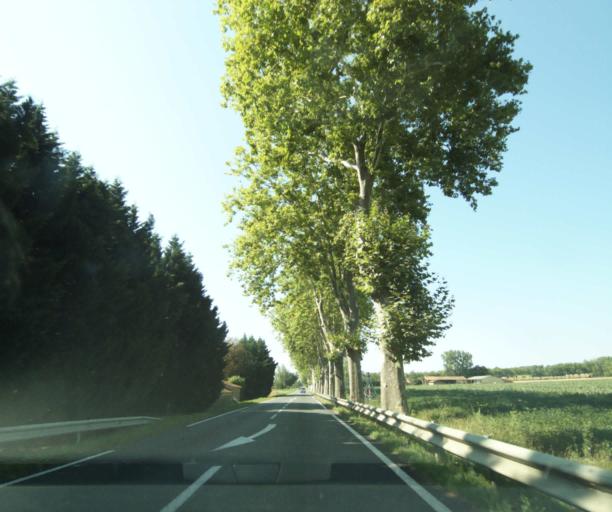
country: FR
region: Midi-Pyrenees
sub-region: Departement de la Haute-Garonne
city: Saint-Sulpice-sur-Leze
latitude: 43.3491
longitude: 1.3249
